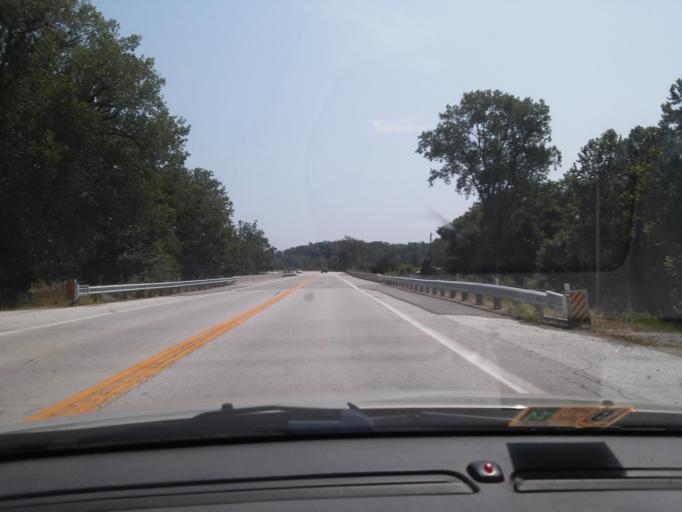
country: US
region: Missouri
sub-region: Pike County
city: Bowling Green
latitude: 39.3791
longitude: -91.1483
